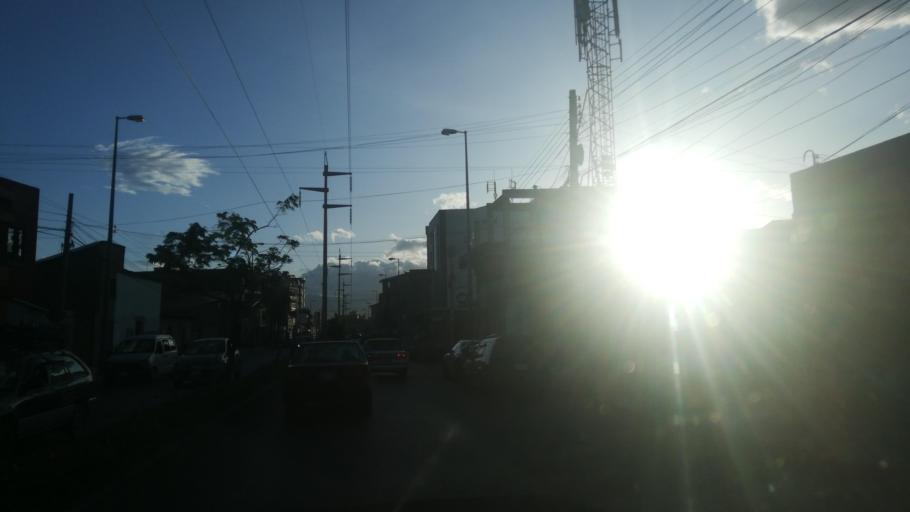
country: BO
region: Cochabamba
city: Cochabamba
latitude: -17.3960
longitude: -66.1824
